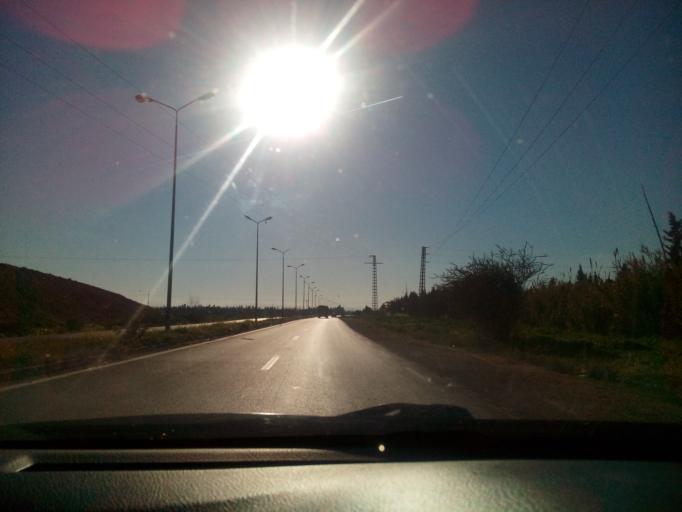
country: DZ
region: Relizane
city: Relizane
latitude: 35.7411
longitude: 0.6063
